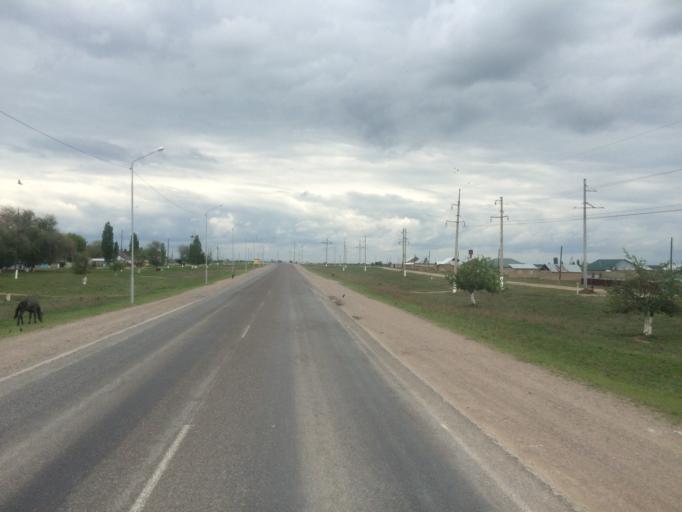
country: KG
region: Chuy
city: Sokuluk
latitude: 43.2478
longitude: 74.2959
